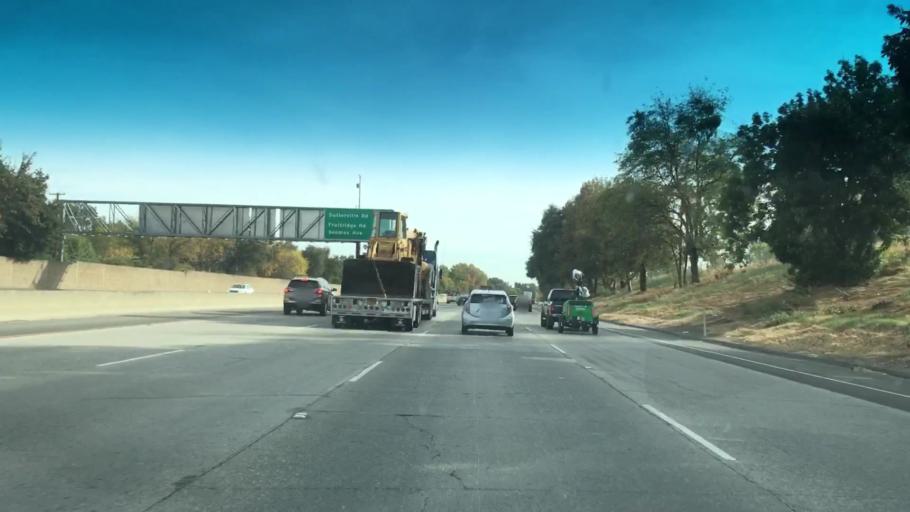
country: US
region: California
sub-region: Yolo County
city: West Sacramento
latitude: 38.5521
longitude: -121.5116
